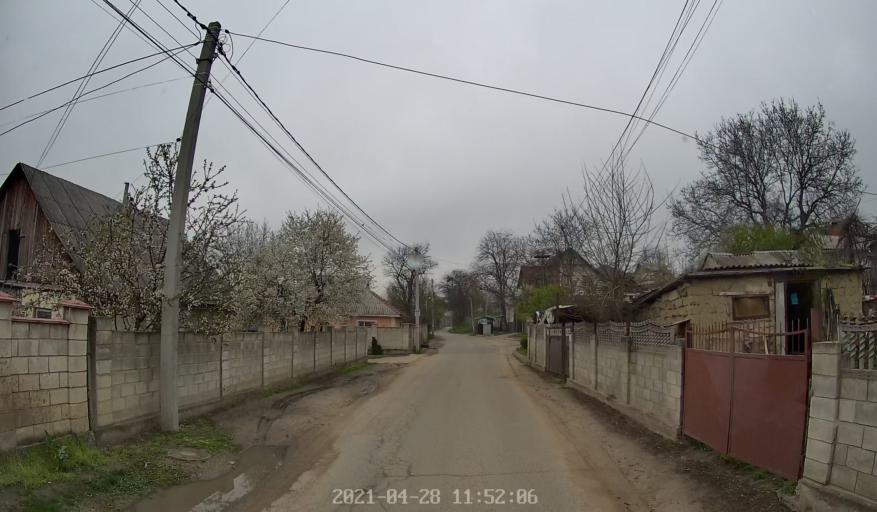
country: MD
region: Chisinau
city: Singera
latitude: 46.9469
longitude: 28.9473
